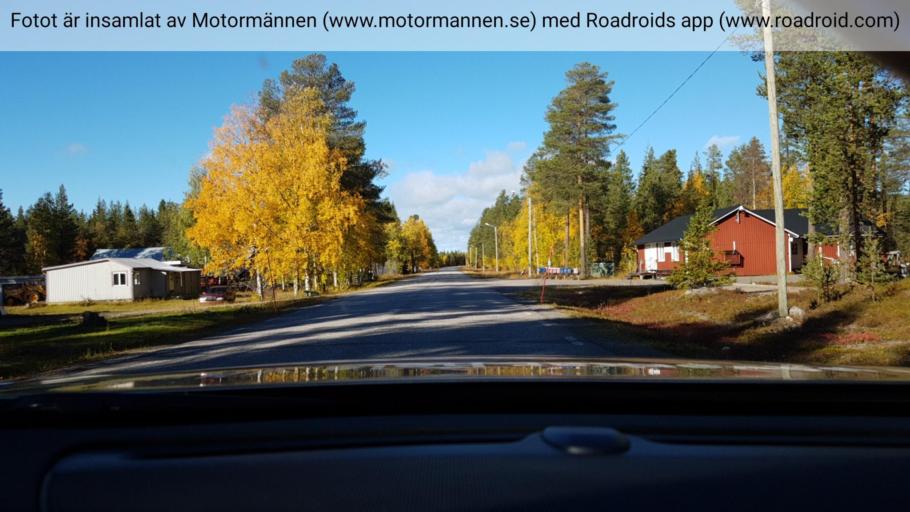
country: SE
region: Norrbotten
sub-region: Arvidsjaurs Kommun
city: Arvidsjaur
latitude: 65.6826
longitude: 18.8087
